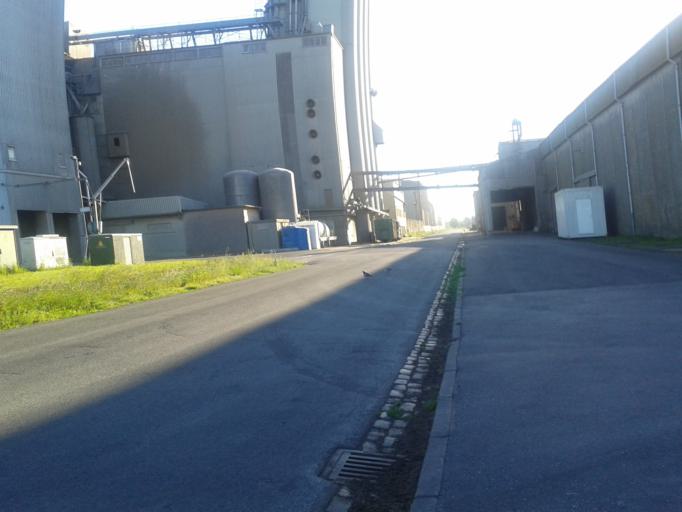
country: DE
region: Schleswig-Holstein
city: Busum
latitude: 54.1249
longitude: 8.8637
